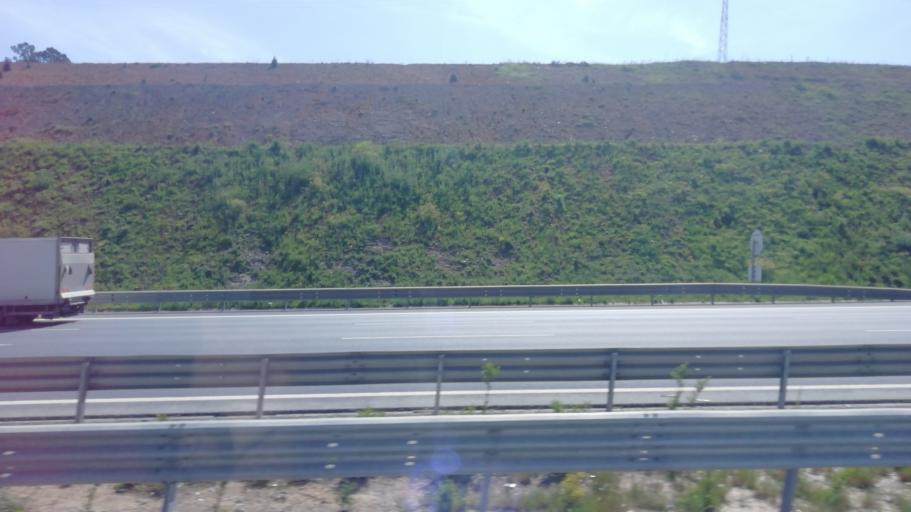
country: TR
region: Istanbul
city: Sancaktepe
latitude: 41.0832
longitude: 29.2834
